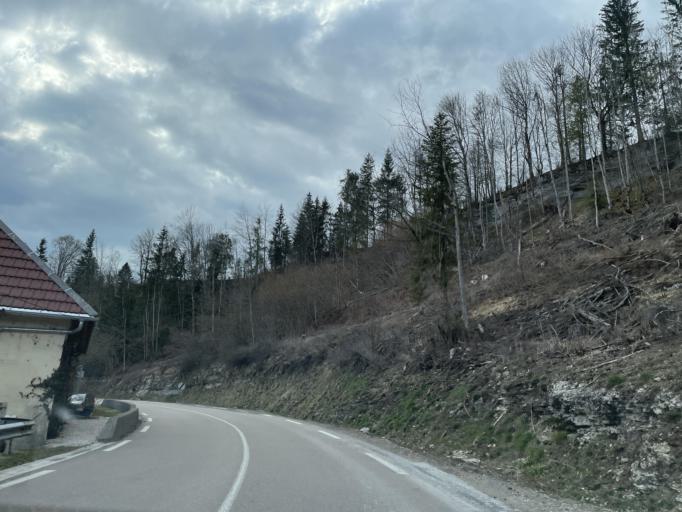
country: FR
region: Franche-Comte
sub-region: Departement du Doubs
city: Gilley
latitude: 47.0349
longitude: 6.5092
